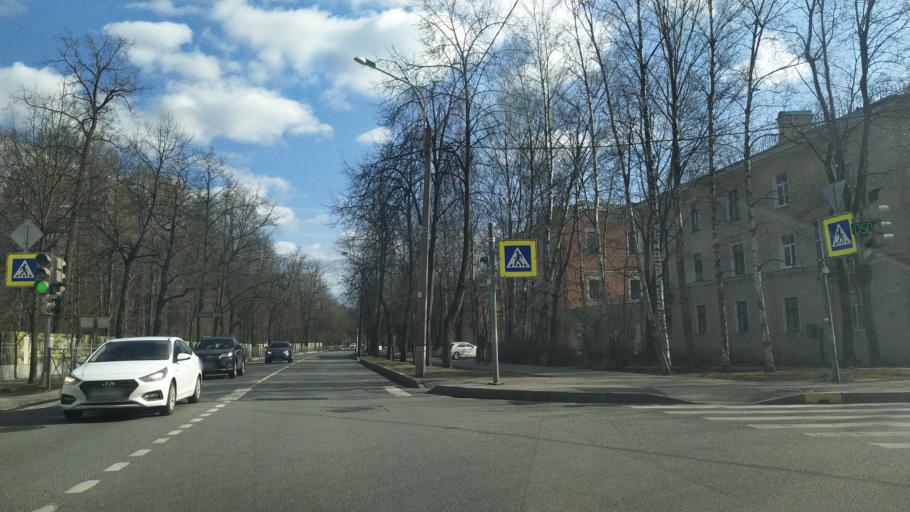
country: RU
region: St.-Petersburg
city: Pushkin
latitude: 59.7088
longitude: 30.4144
